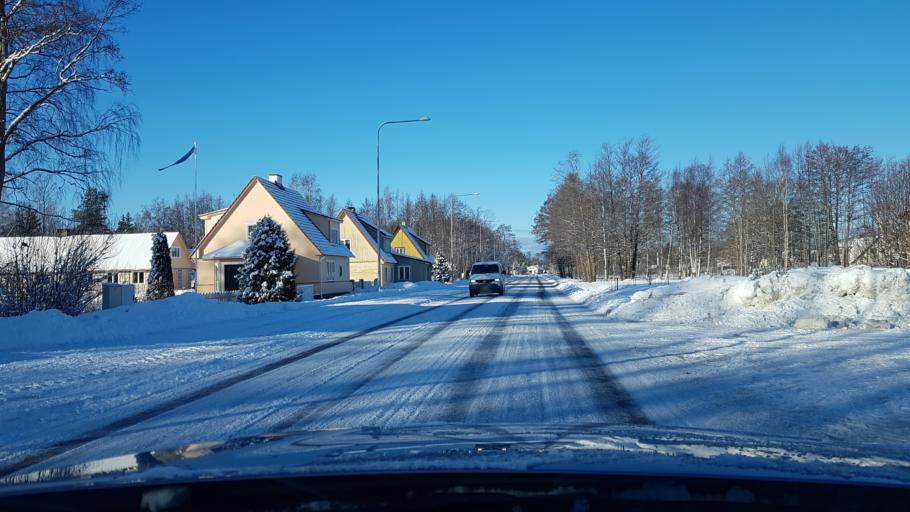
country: EE
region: Hiiumaa
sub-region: Kaerdla linn
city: Kardla
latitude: 58.9873
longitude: 22.7530
